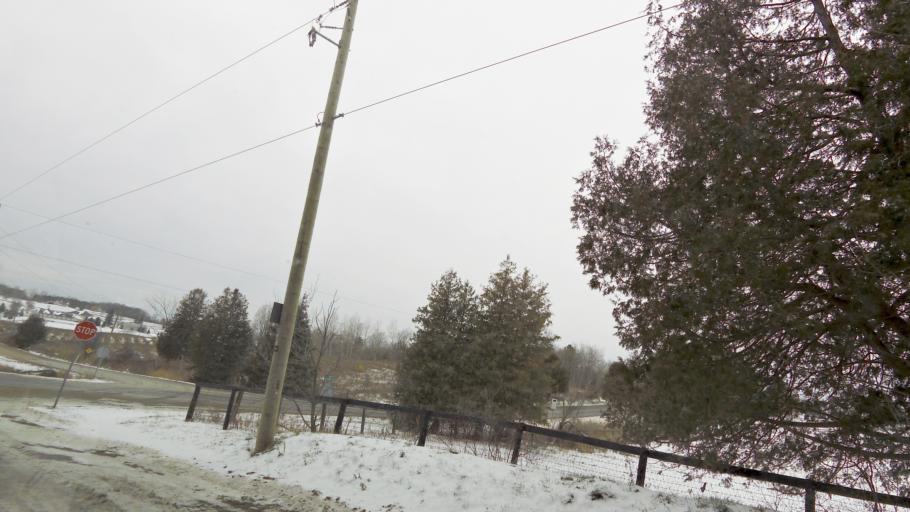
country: CA
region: Ontario
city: Bradford West Gwillimbury
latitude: 43.9619
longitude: -79.6410
